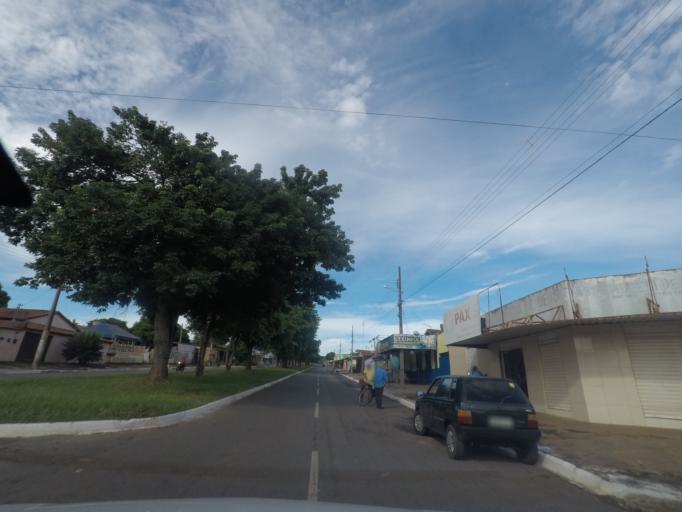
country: BR
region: Goias
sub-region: Aparecida De Goiania
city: Aparecida de Goiania
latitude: -16.8204
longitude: -49.3076
